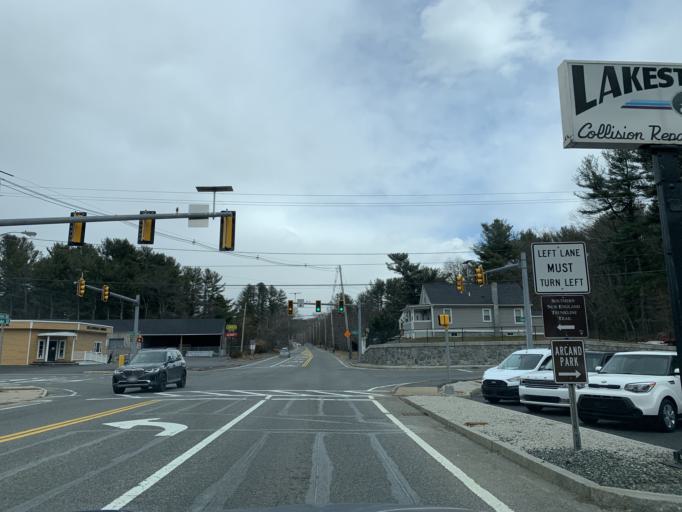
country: US
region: Massachusetts
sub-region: Norfolk County
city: Bellingham
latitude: 42.0359
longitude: -71.4671
